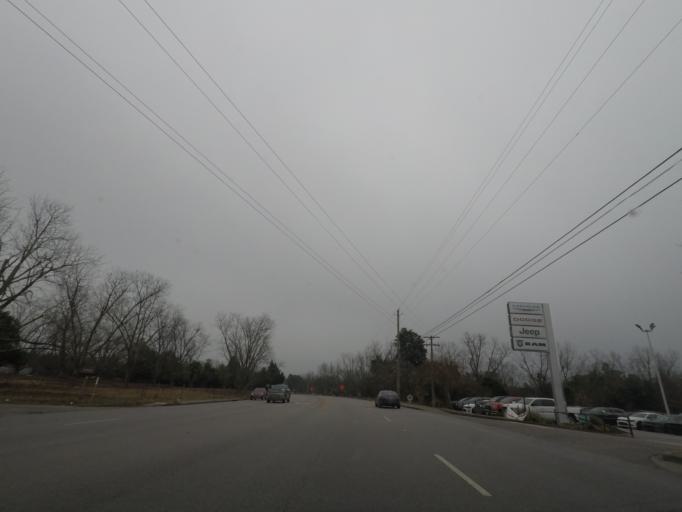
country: US
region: South Carolina
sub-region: Clarendon County
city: Manning
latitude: 33.7000
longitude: -80.2367
